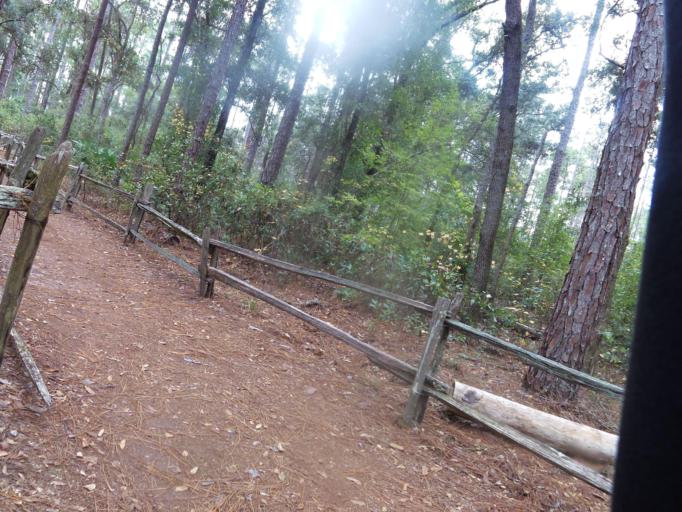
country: US
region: Georgia
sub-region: Charlton County
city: Folkston
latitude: 30.7148
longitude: -82.1561
